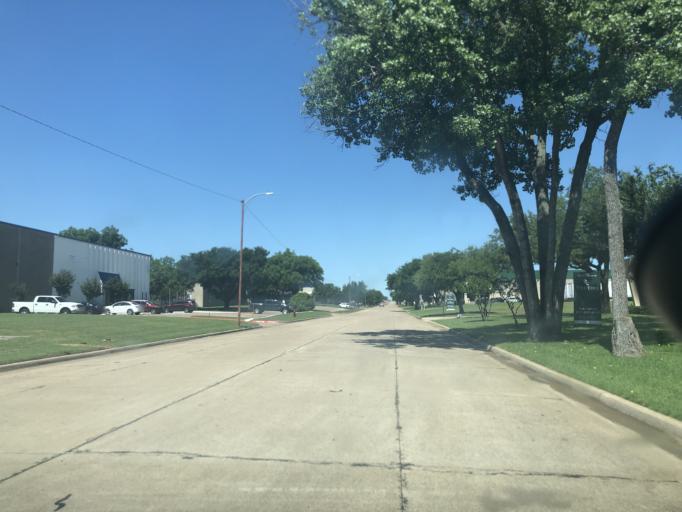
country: US
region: Texas
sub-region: Dallas County
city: Grand Prairie
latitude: 32.7829
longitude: -97.0410
